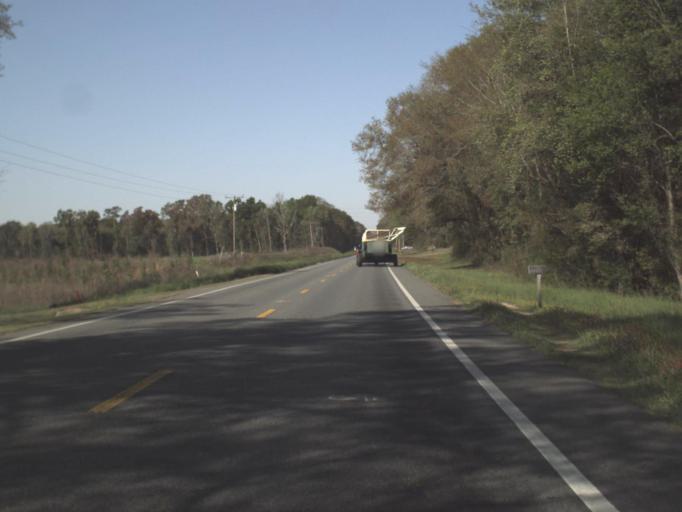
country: US
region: Florida
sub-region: Jackson County
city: Malone
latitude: 30.9485
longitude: -85.2526
